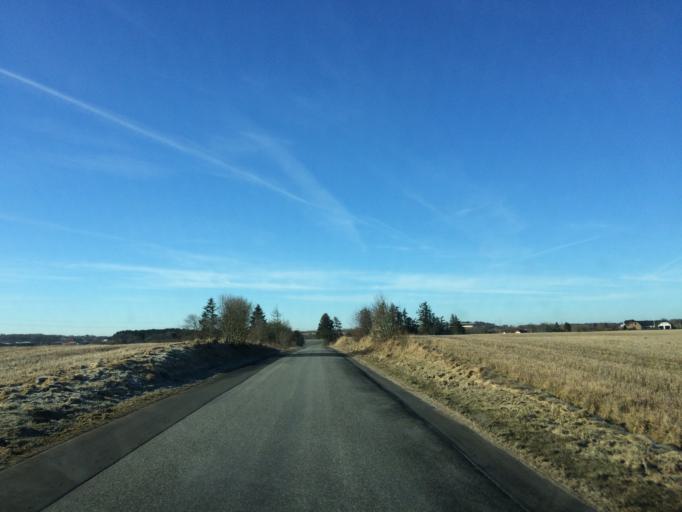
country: DK
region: North Denmark
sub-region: Mariagerfjord Kommune
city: Hobro
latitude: 56.6063
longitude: 9.6328
